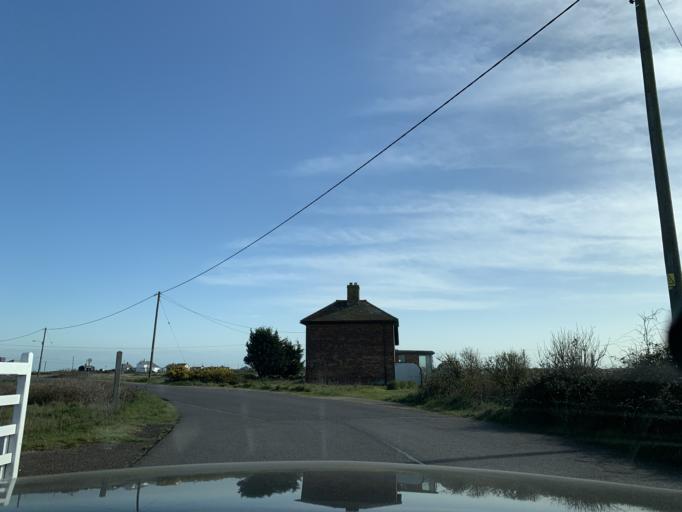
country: GB
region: England
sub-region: Kent
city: New Romney
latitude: 50.9282
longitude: 0.9712
